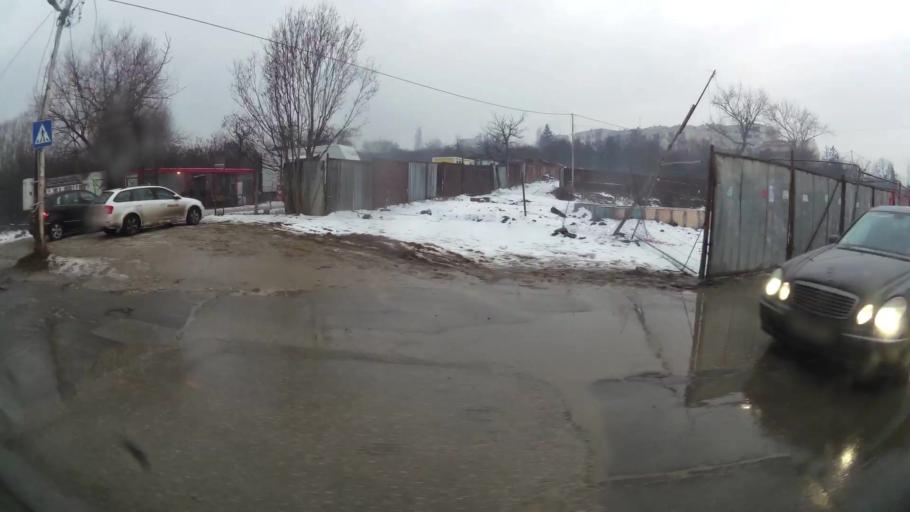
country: BG
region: Sofia-Capital
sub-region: Stolichna Obshtina
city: Sofia
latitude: 42.6833
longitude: 23.2558
